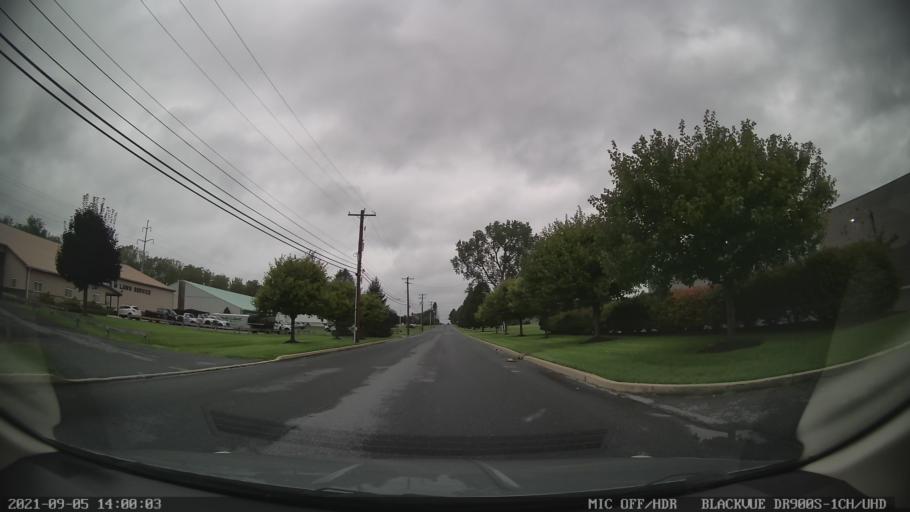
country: US
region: Pennsylvania
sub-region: Lehigh County
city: Whitehall Township
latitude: 40.6746
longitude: -75.5053
